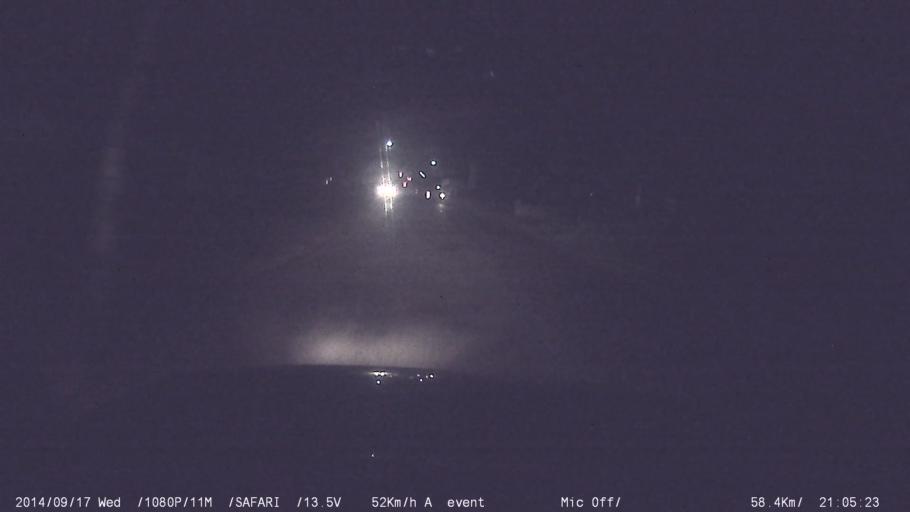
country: IN
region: Kerala
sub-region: Kottayam
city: Changanacheri
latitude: 9.4885
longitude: 76.5248
